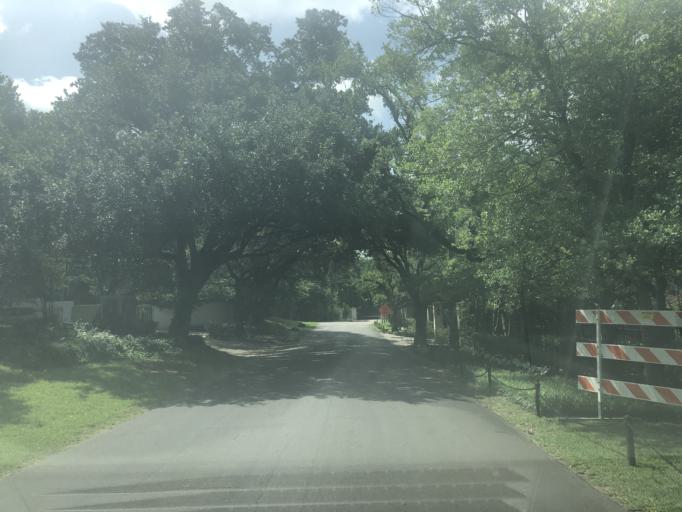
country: US
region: Texas
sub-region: Dallas County
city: University Park
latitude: 32.8672
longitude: -96.8266
